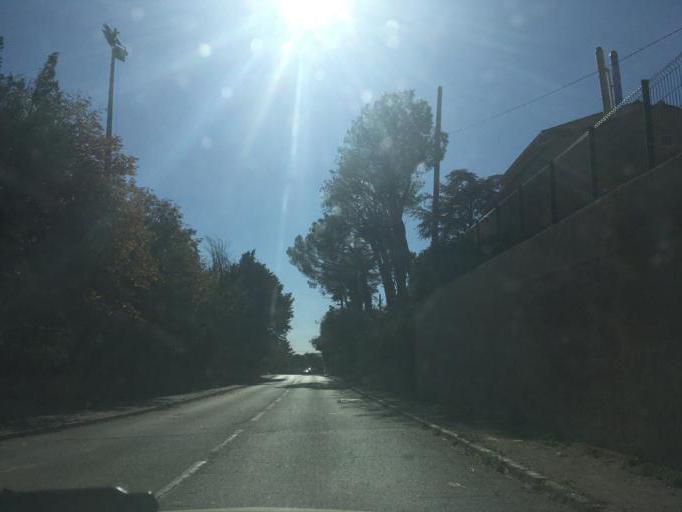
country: FR
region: Provence-Alpes-Cote d'Azur
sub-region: Departement du Var
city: La Garde-Freinet
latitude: 43.3145
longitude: 6.4712
